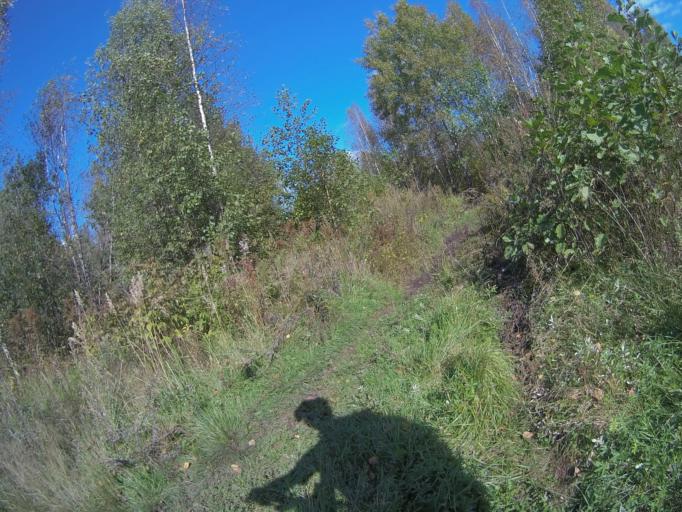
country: RU
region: Vladimir
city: Raduzhnyy
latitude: 55.9394
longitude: 40.2356
